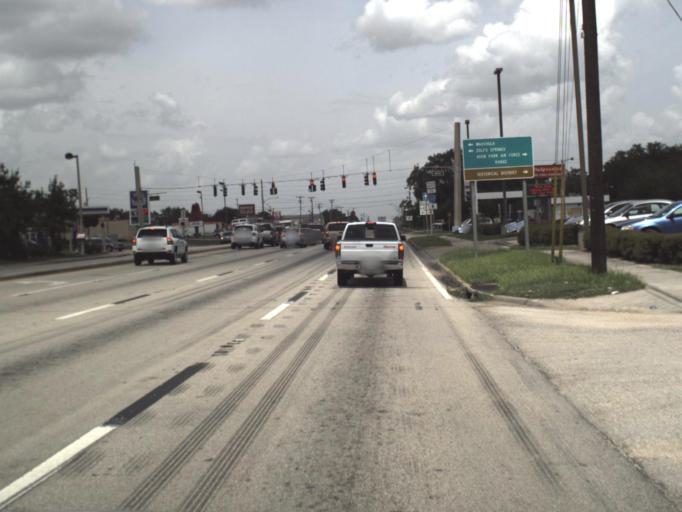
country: US
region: Florida
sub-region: Highlands County
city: Avon Park
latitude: 27.5946
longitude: -81.5143
